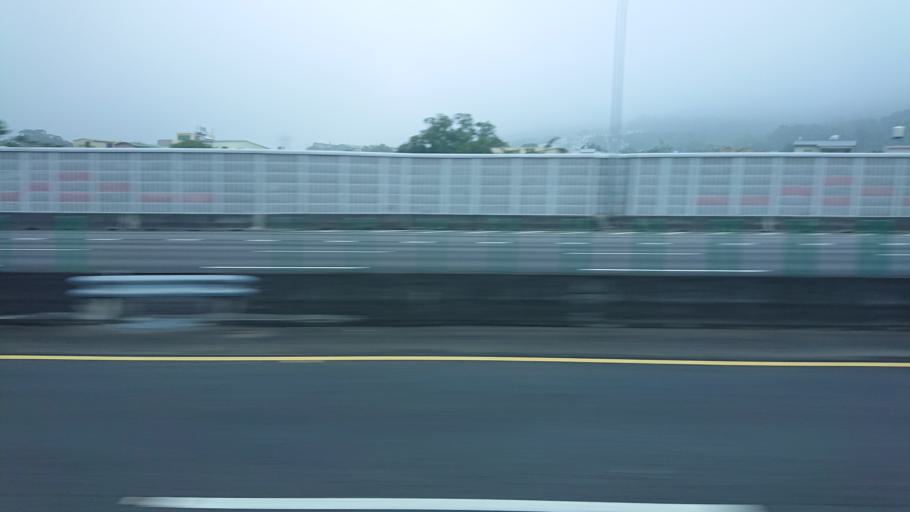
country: TW
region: Taiwan
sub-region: Miaoli
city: Miaoli
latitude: 24.4710
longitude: 120.7874
